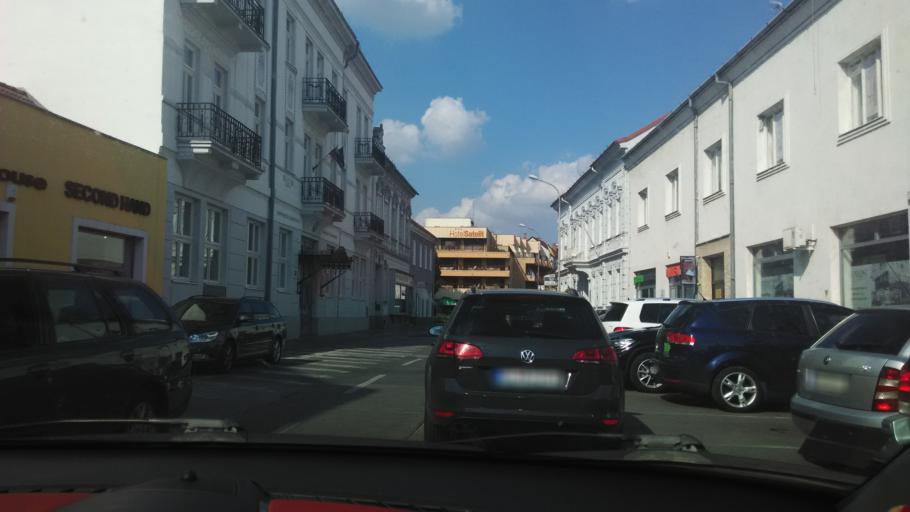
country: SK
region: Trnavsky
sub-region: Okres Trnava
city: Piestany
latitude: 48.5892
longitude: 17.8341
